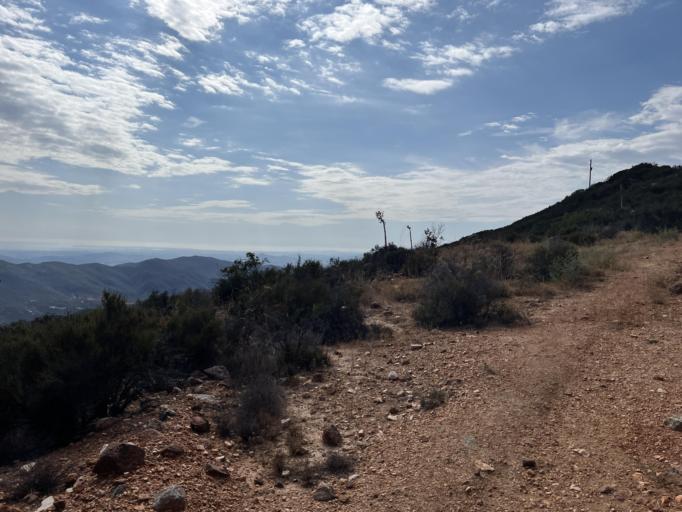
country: US
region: California
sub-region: San Diego County
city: Harbison Canyon
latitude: 32.7537
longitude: -116.8051
